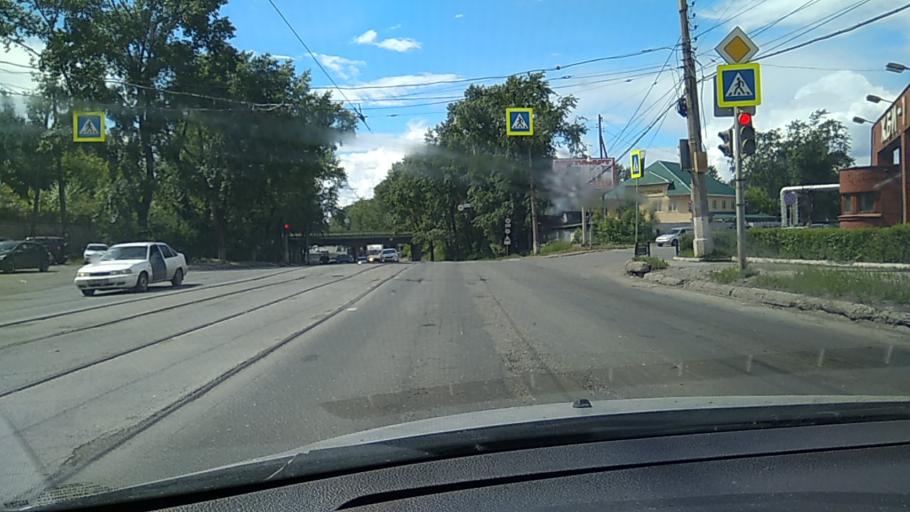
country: RU
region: Sverdlovsk
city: Nizhniy Tagil
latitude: 57.9299
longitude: 60.0025
